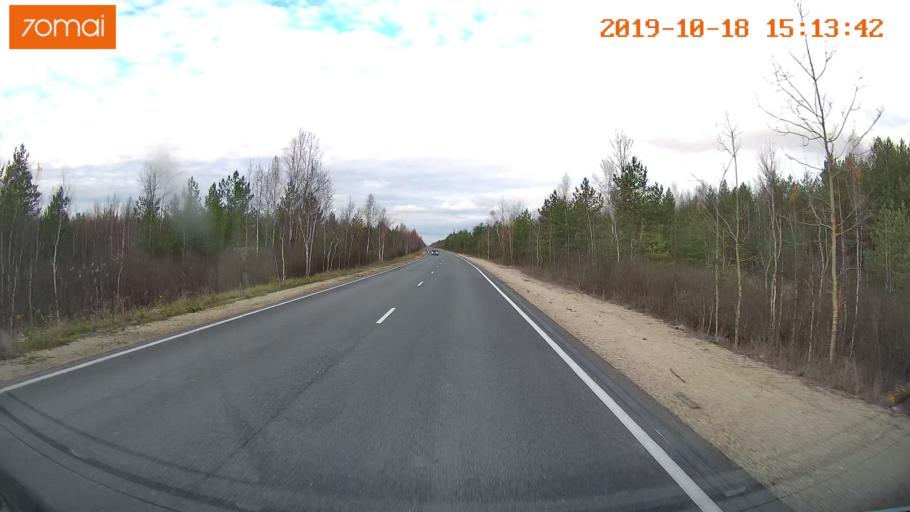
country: RU
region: Vladimir
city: Gus'-Khrustal'nyy
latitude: 55.5909
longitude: 40.7186
